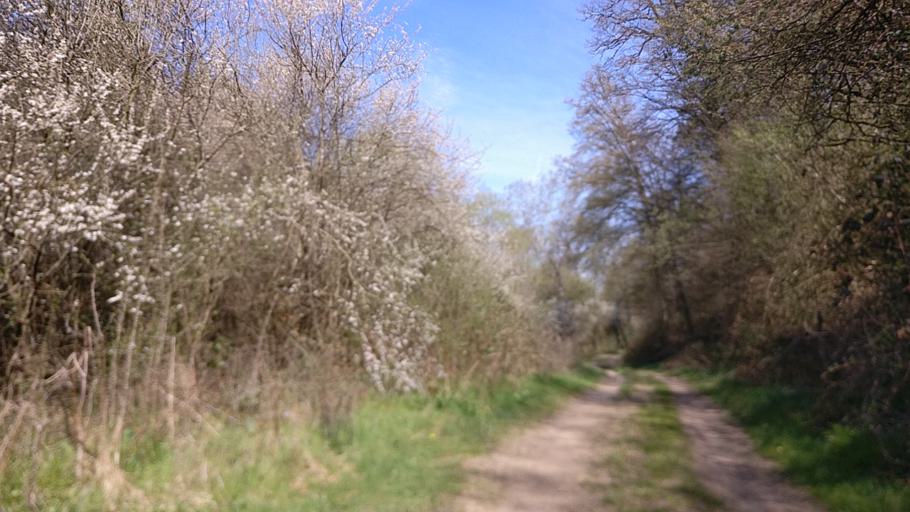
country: DE
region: Rheinland-Pfalz
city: Peterslahr
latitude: 50.6377
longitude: 7.4405
